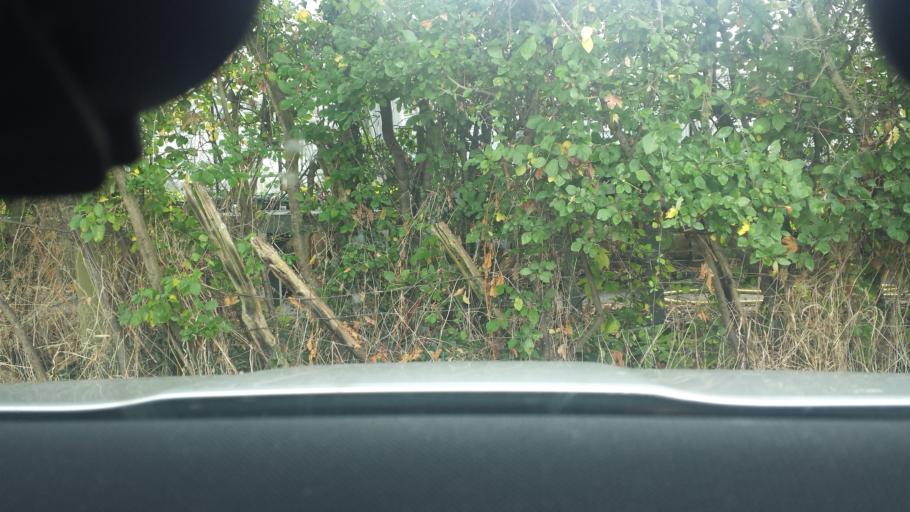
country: GB
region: England
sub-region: Kent
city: Staplehurst
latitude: 51.1813
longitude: 0.5473
